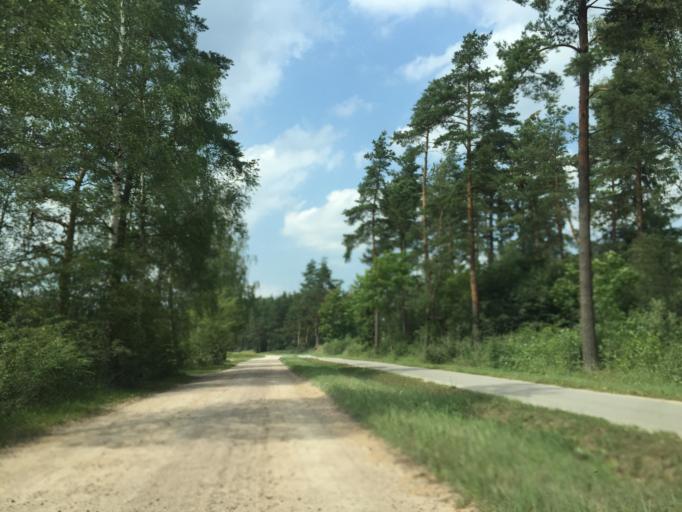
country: LV
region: Olaine
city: Olaine
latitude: 56.7778
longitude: 23.9006
